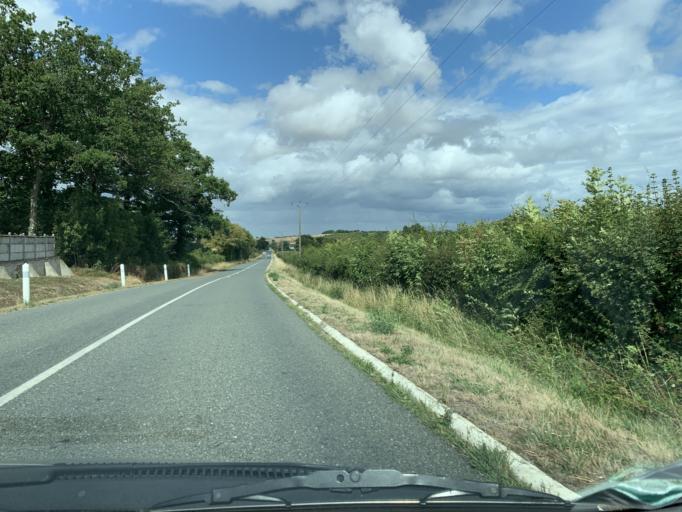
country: FR
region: Bourgogne
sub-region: Departement de la Nievre
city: Varzy
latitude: 47.3946
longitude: 3.4449
